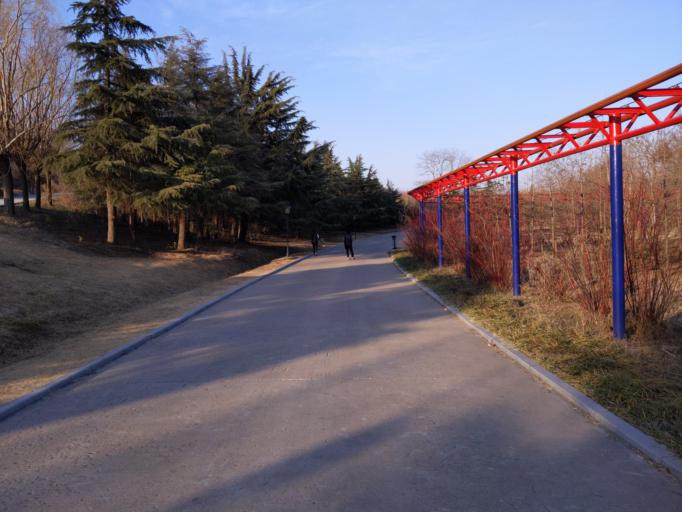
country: CN
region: Henan Sheng
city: Puyang
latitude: 35.7785
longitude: 114.9505
